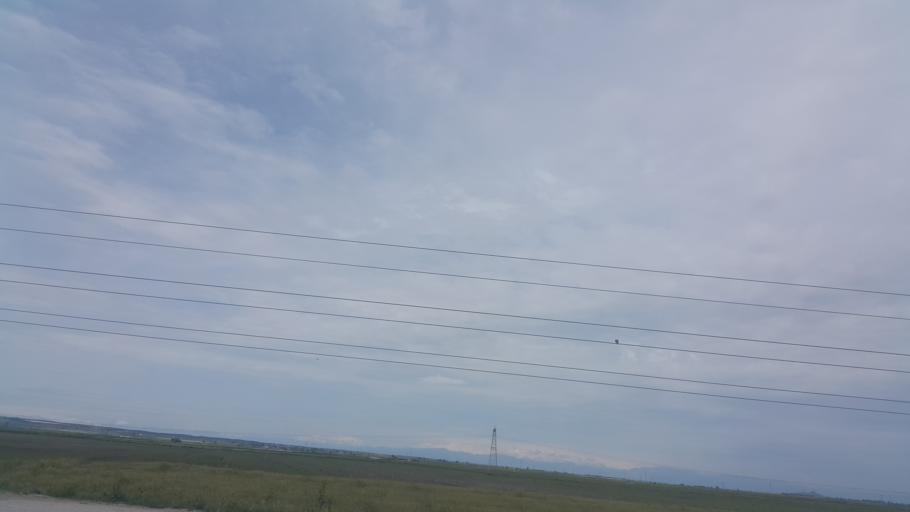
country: TR
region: Adana
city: Ceyhan
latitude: 37.0242
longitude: 35.7282
